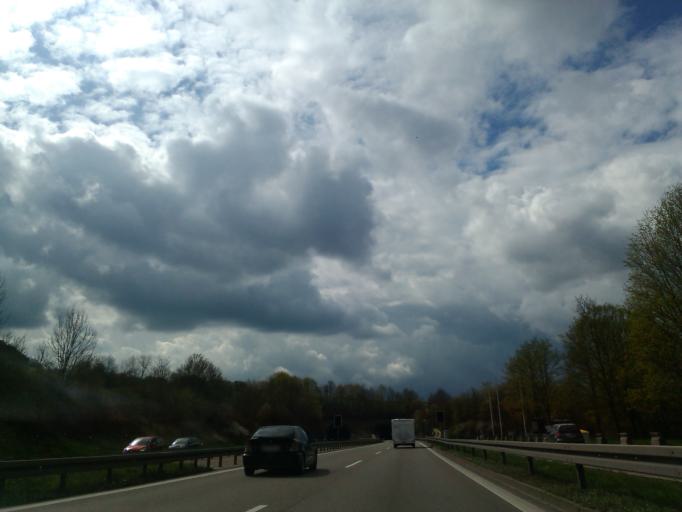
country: DE
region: Baden-Wuerttemberg
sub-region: Tuebingen Region
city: Ulm
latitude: 48.4182
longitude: 9.9723
